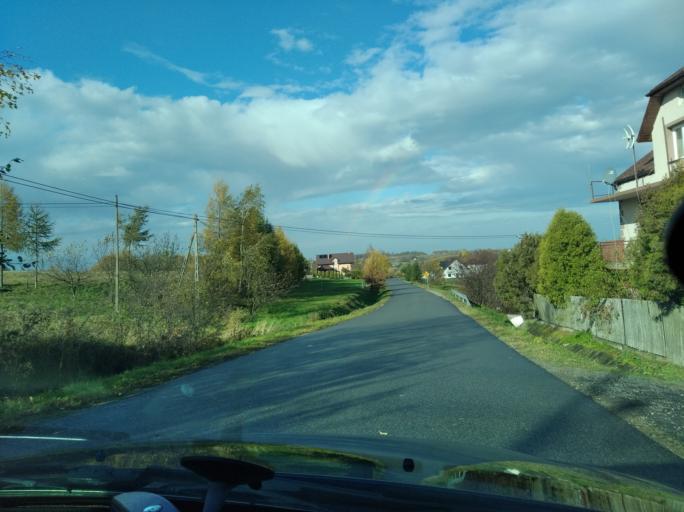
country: PL
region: Subcarpathian Voivodeship
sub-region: Powiat ropczycko-sedziszowski
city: Niedzwiada
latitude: 50.0133
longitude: 21.4802
